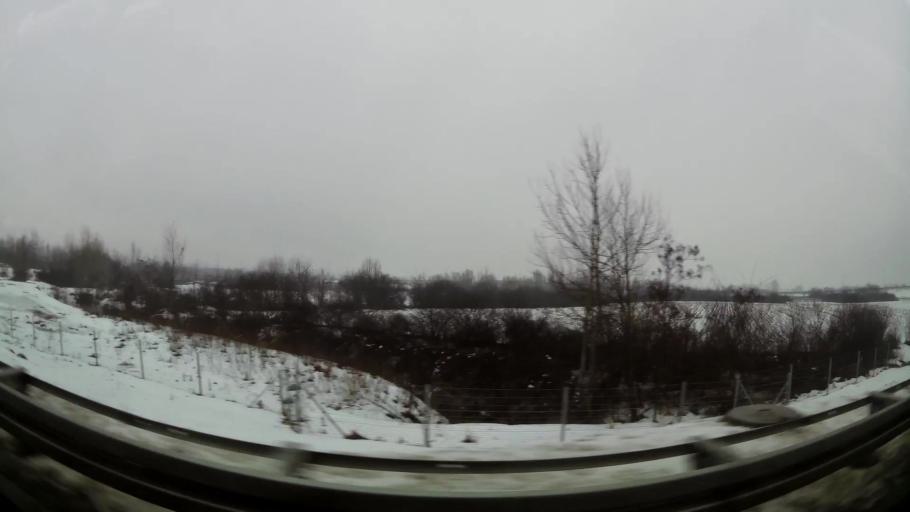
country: RS
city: Ostruznica
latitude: 44.7345
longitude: 20.3326
